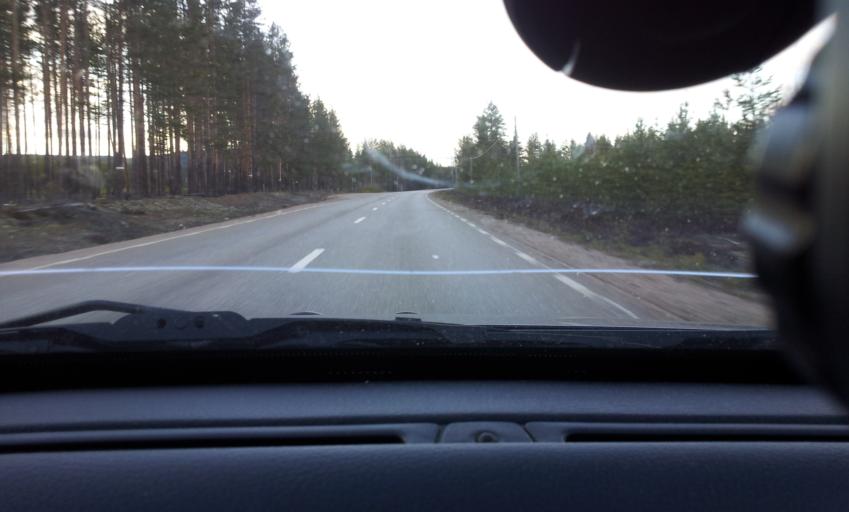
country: SE
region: Vaesternorrland
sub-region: Ange Kommun
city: Ange
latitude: 62.0655
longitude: 15.1086
